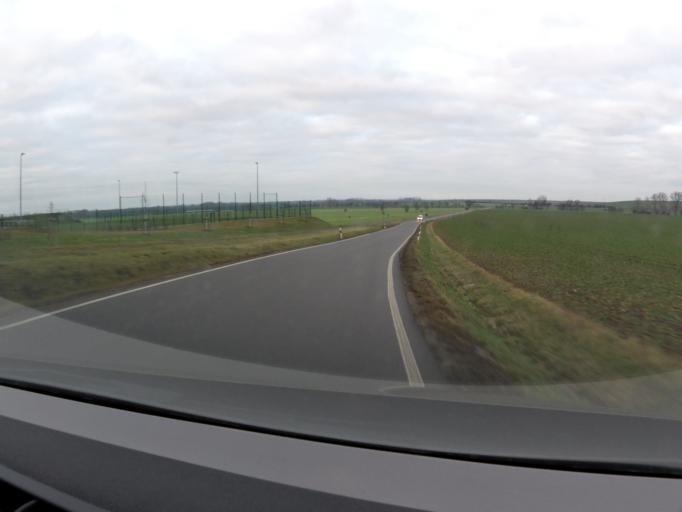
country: DE
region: Thuringia
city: Apfelstadt
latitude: 50.8667
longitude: 10.8929
